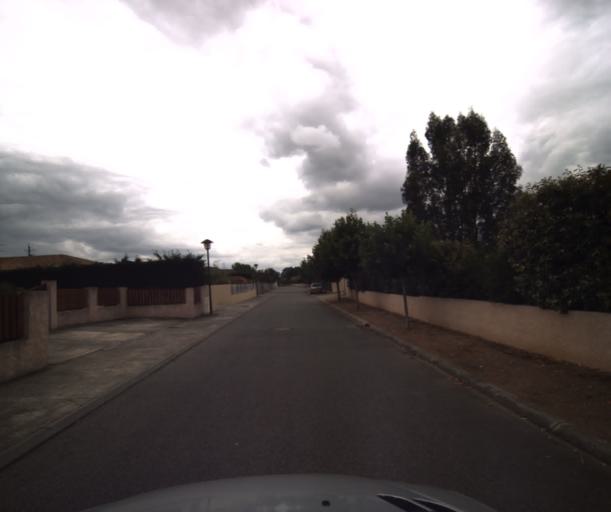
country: FR
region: Midi-Pyrenees
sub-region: Departement de la Haute-Garonne
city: Labarthe-sur-Leze
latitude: 43.4595
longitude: 1.4062
